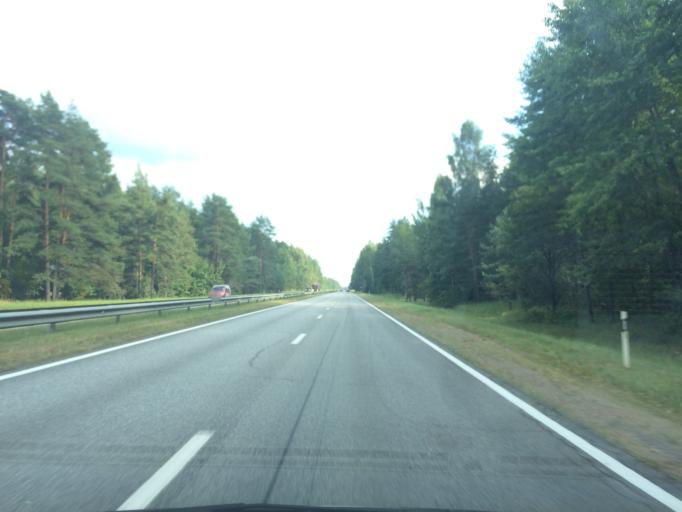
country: LV
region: Ikskile
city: Ikskile
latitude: 56.8334
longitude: 24.5063
